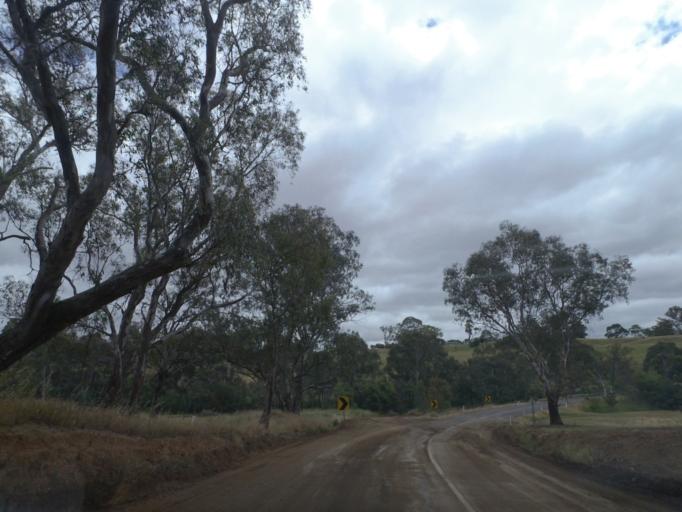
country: AU
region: Victoria
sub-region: Whittlesea
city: Whittlesea
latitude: -37.1119
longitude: 145.0233
